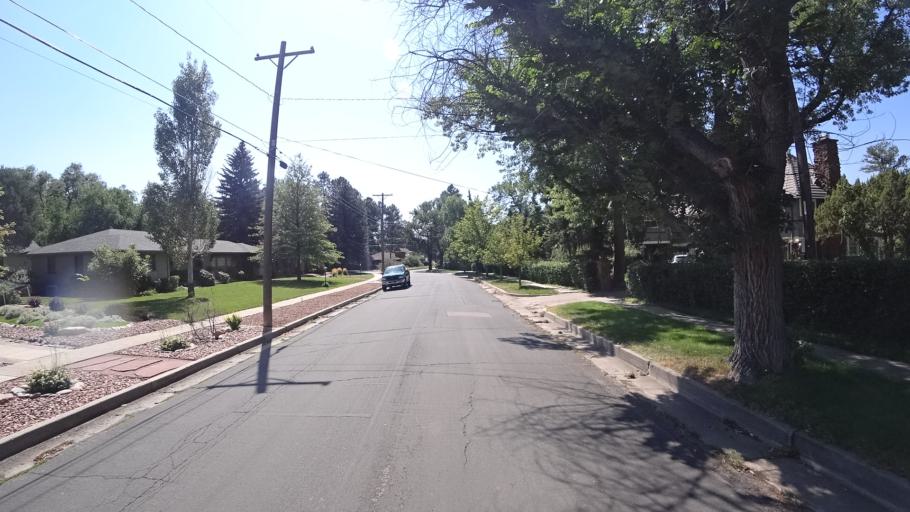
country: US
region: Colorado
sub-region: El Paso County
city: Colorado Springs
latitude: 38.8548
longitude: -104.8289
